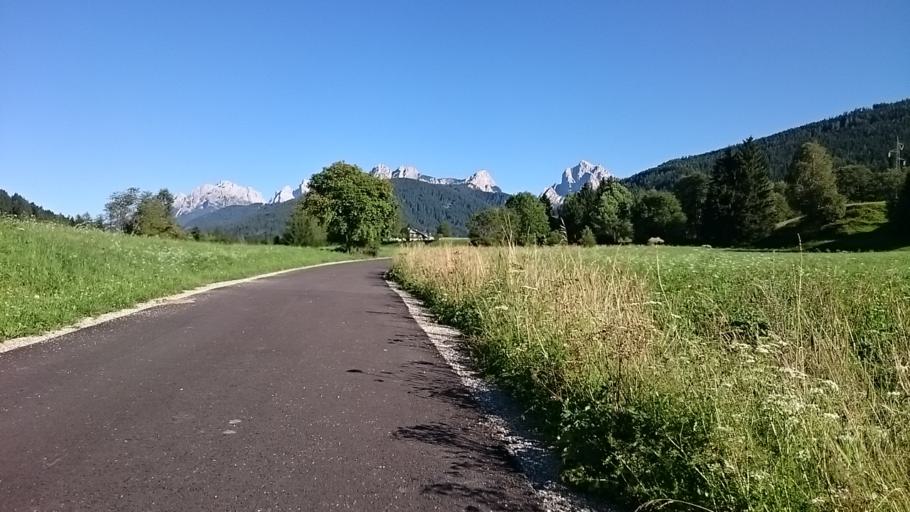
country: IT
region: Trentino-Alto Adige
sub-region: Bolzano
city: Monguelfo
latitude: 46.7481
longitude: 12.1179
